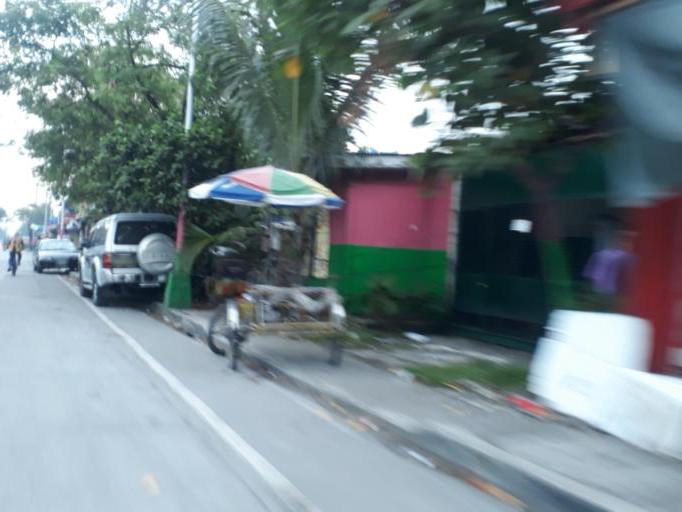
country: PH
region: Calabarzon
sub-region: Province of Rizal
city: Valenzuela
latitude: 14.6874
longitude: 120.9575
